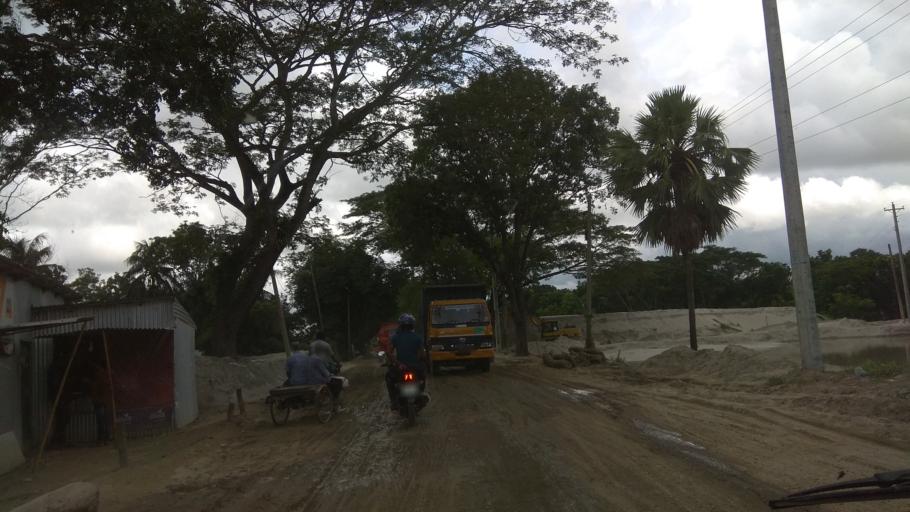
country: BD
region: Khulna
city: Kalia
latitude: 23.1968
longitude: 89.6965
